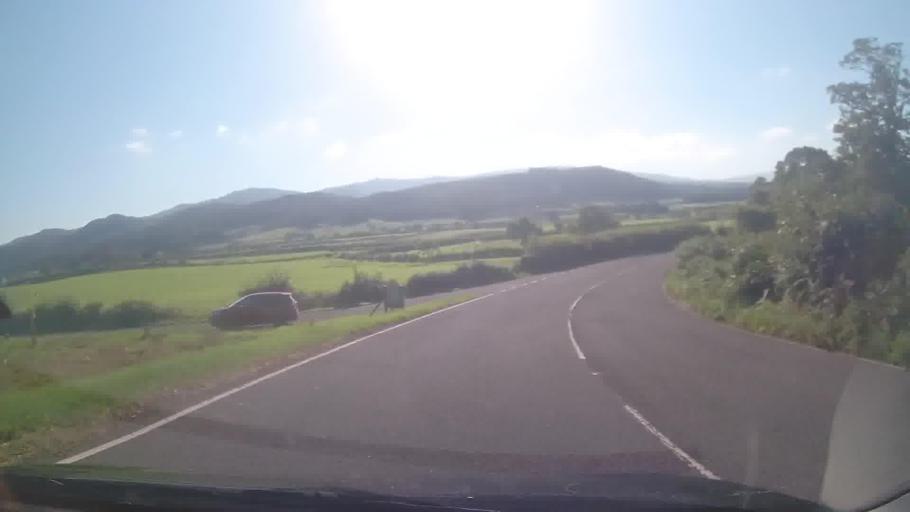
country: GB
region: England
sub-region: Cumbria
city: Seascale
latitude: 54.3613
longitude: -3.3718
